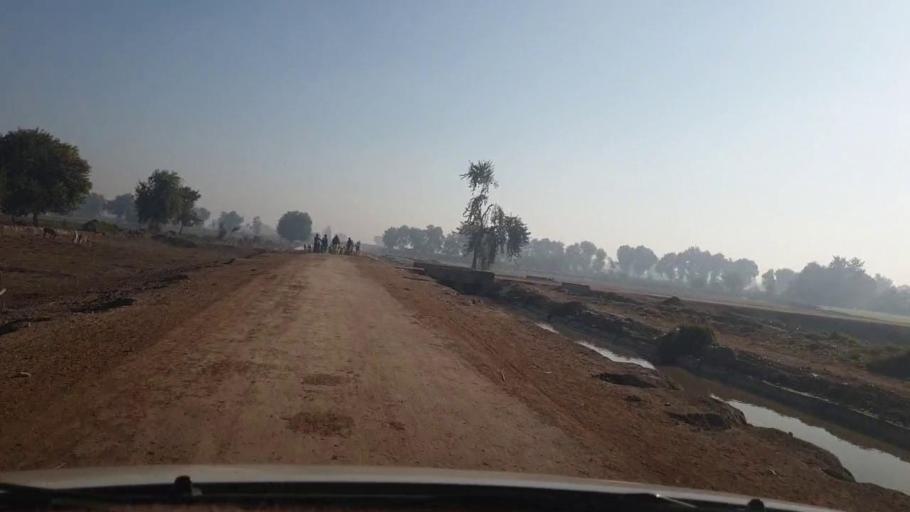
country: PK
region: Sindh
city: Dadu
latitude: 26.6841
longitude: 67.7937
